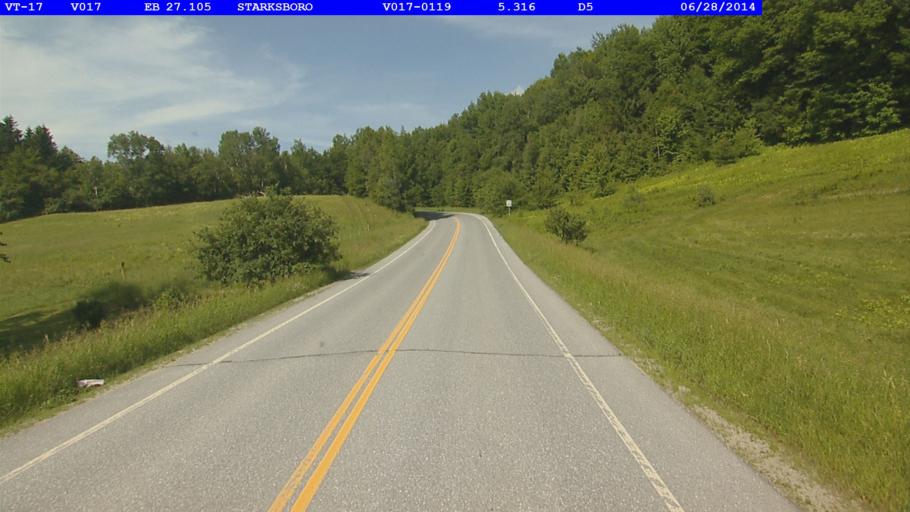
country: US
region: Vermont
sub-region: Addison County
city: Bristol
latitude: 44.2154
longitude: -72.9637
